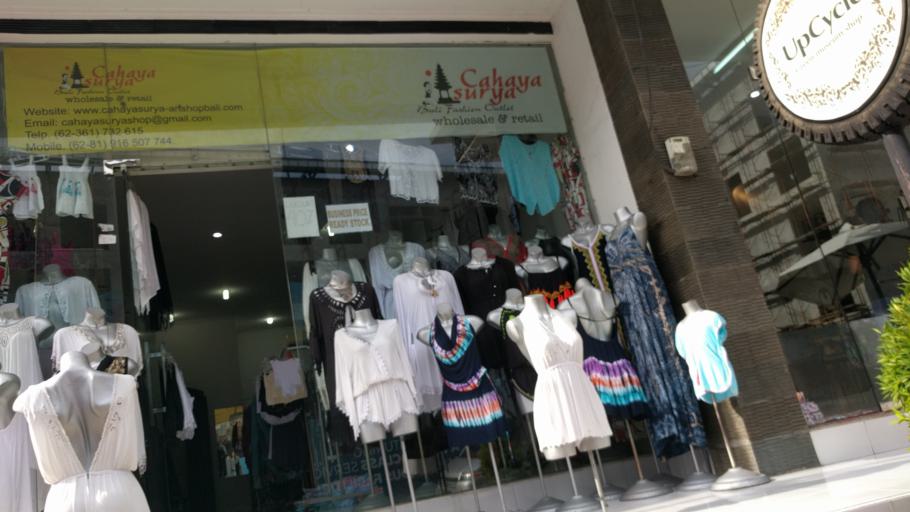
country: ID
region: Bali
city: Kuta
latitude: -8.6972
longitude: 115.1678
